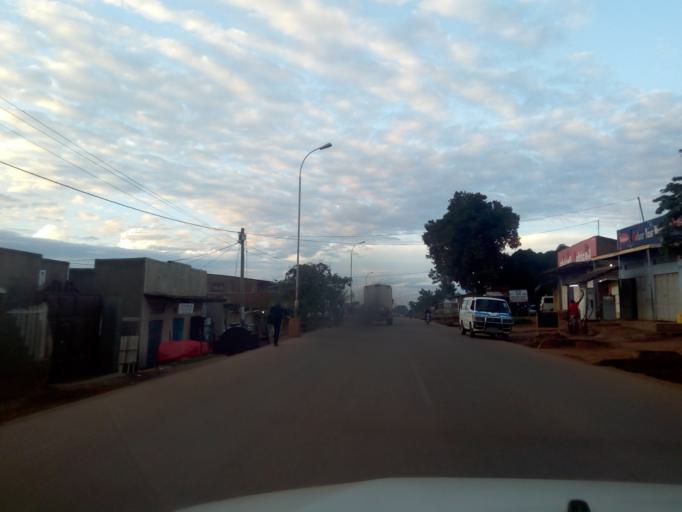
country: UG
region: Central Region
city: Kampala Central Division
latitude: 0.3717
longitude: 32.5688
